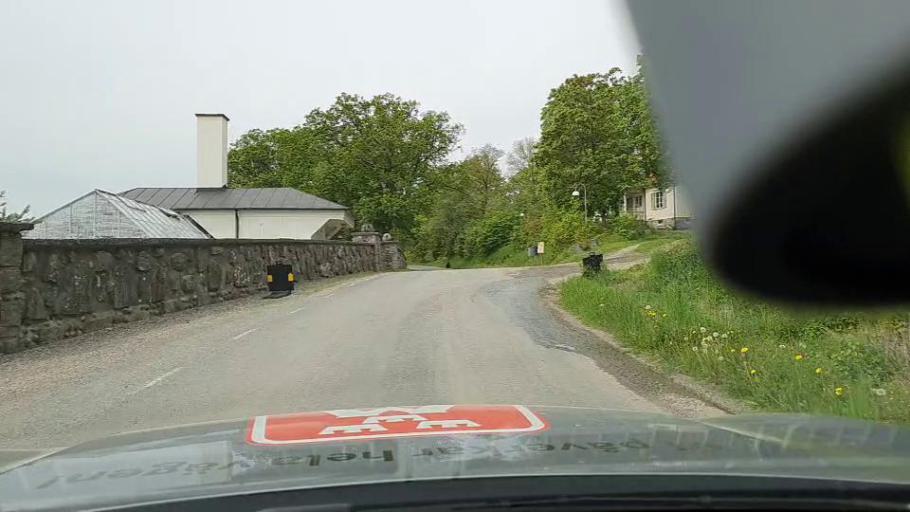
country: SE
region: Soedermanland
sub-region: Flens Kommun
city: Halleforsnas
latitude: 59.0997
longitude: 16.4852
